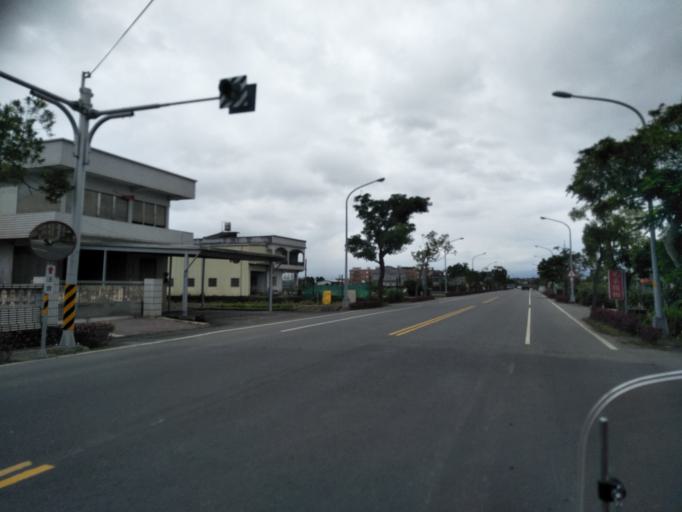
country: TW
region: Taiwan
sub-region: Yilan
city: Yilan
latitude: 24.7960
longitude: 121.7859
